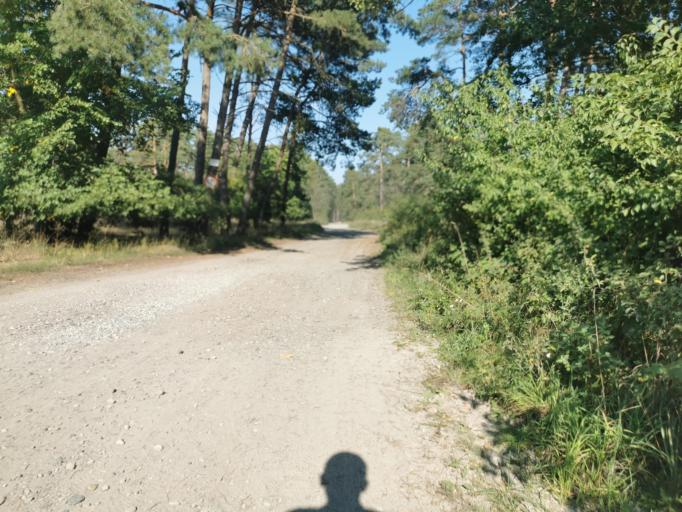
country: SK
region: Trnavsky
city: Gbely
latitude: 48.6388
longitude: 17.2269
